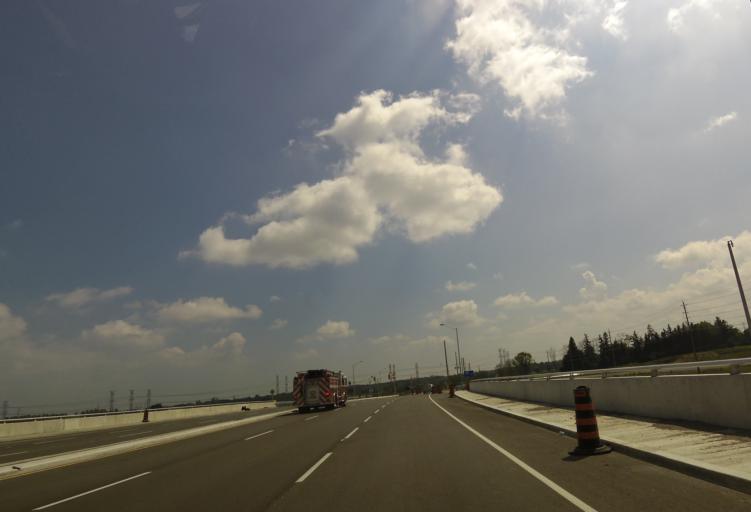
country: CA
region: Ontario
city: Oshawa
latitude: 43.9479
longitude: -78.9603
